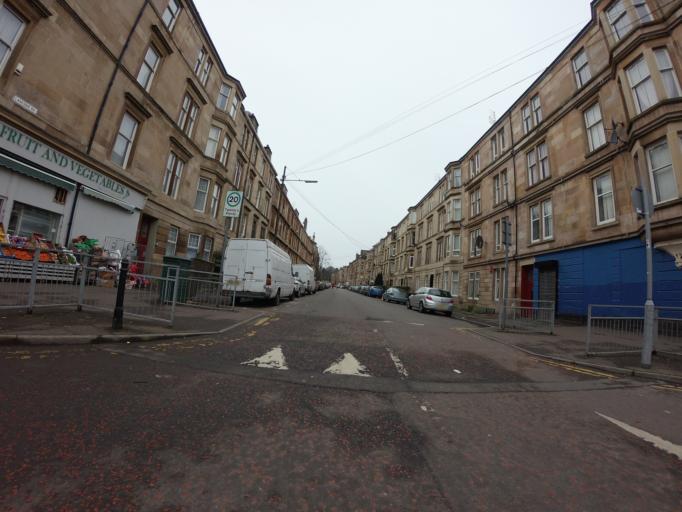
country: GB
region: Scotland
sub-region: Glasgow City
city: Glasgow
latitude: 55.8361
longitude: -4.2623
